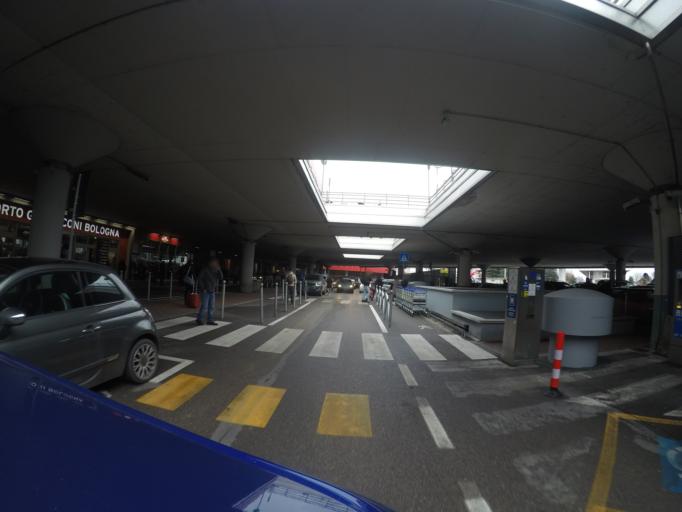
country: IT
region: Emilia-Romagna
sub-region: Provincia di Bologna
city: Trebbo
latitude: 44.5292
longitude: 11.2931
